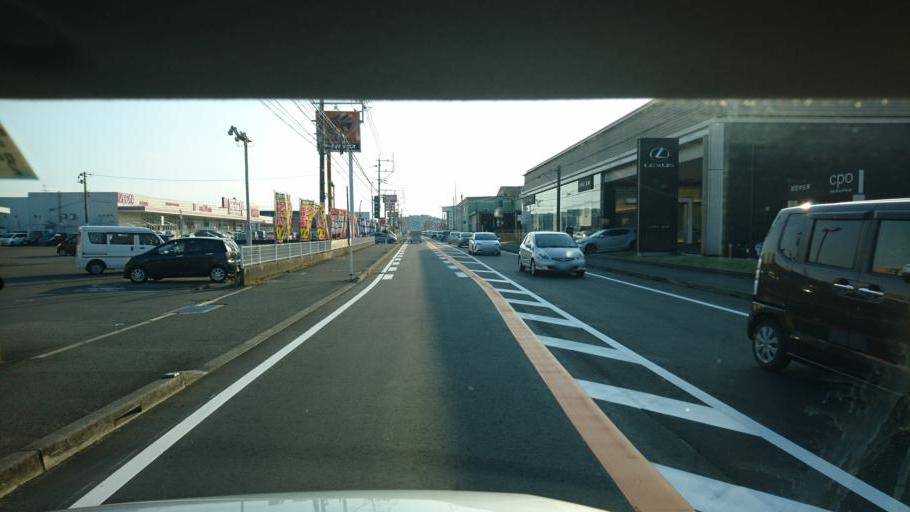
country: JP
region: Miyazaki
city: Miyazaki-shi
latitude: 31.9818
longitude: 131.4470
